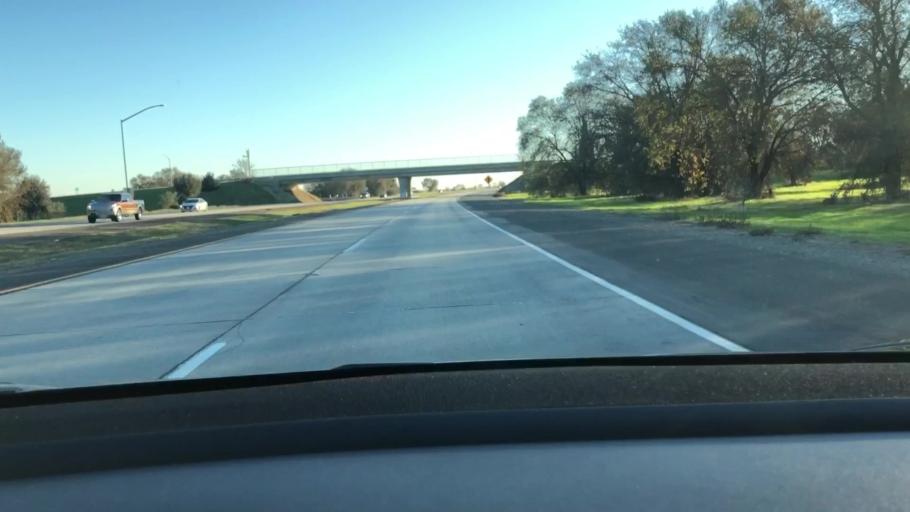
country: US
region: California
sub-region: Yolo County
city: Woodland
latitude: 38.6647
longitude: -121.7515
